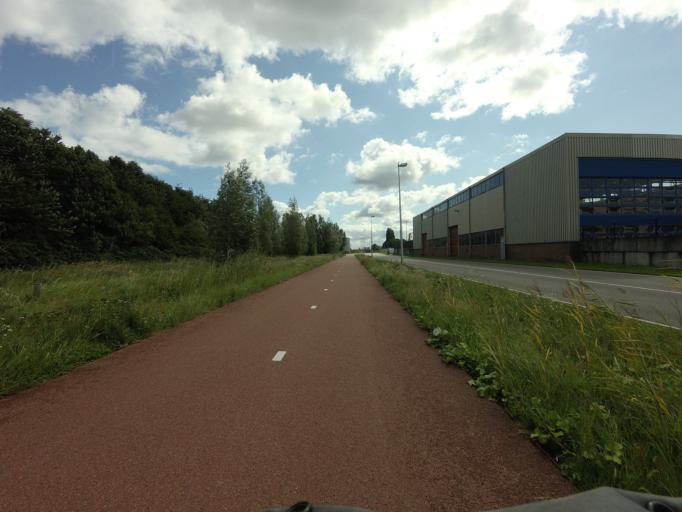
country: NL
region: Utrecht
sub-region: Gemeente Nieuwegein
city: Nieuwegein
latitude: 52.0799
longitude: 5.0544
